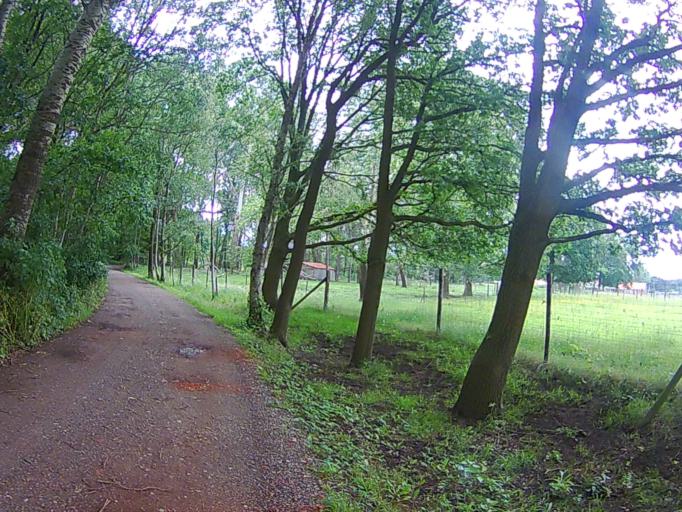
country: BE
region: Flanders
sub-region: Provincie Antwerpen
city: Berlaar
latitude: 51.1178
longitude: 4.6908
